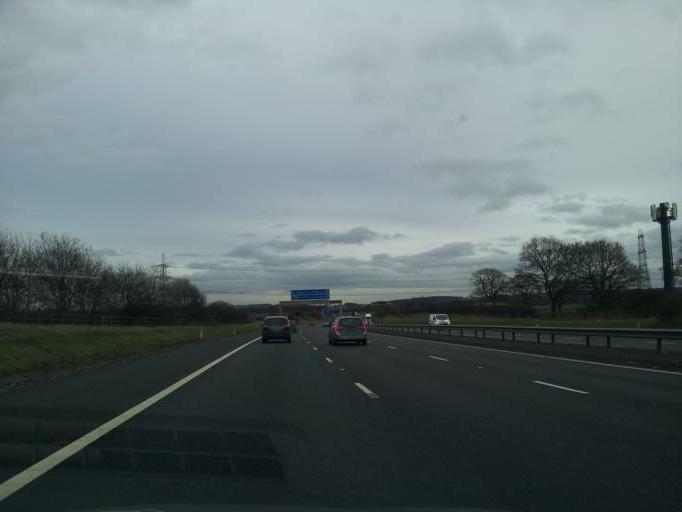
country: GB
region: England
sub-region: Staffordshire
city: Shenstone
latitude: 52.6525
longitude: -1.8483
